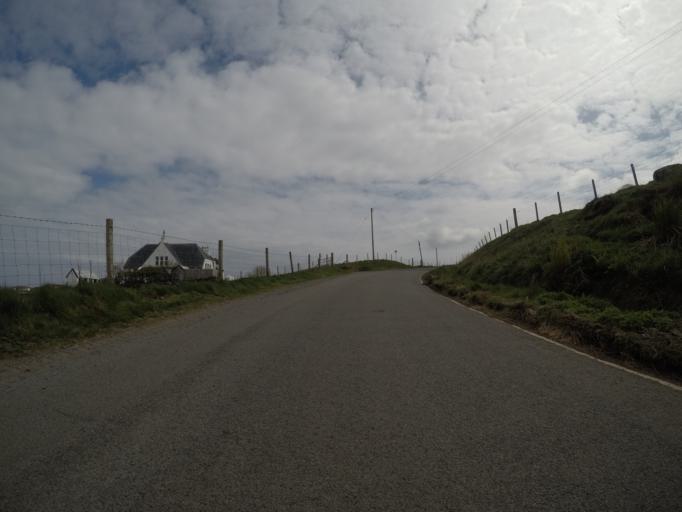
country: GB
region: Scotland
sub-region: Highland
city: Portree
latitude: 57.6838
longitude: -6.3011
